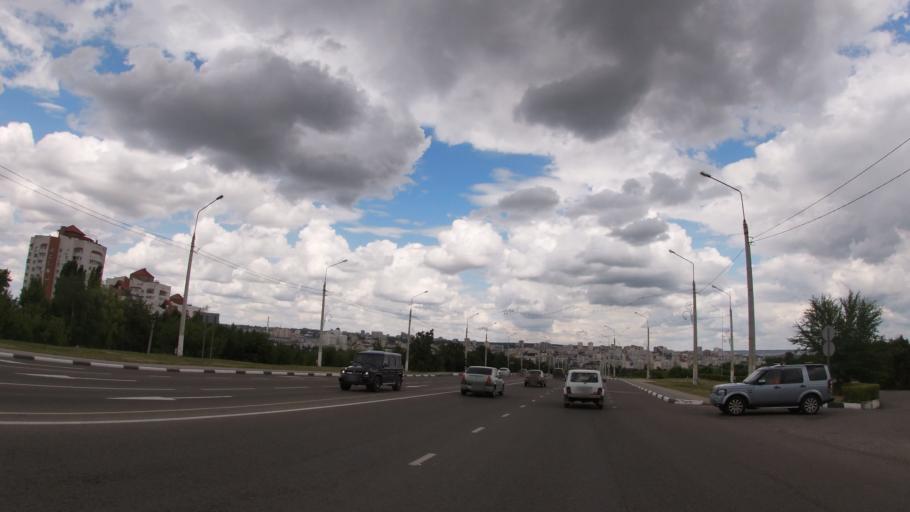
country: RU
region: Belgorod
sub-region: Belgorodskiy Rayon
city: Belgorod
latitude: 50.5810
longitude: 36.5832
